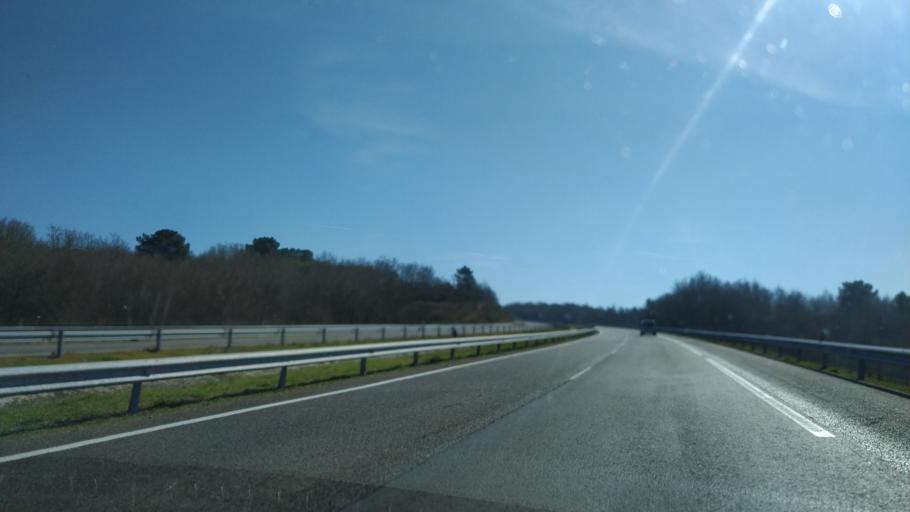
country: ES
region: Galicia
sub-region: Provincia de Ourense
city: Taboadela
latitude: 42.2197
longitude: -7.8434
